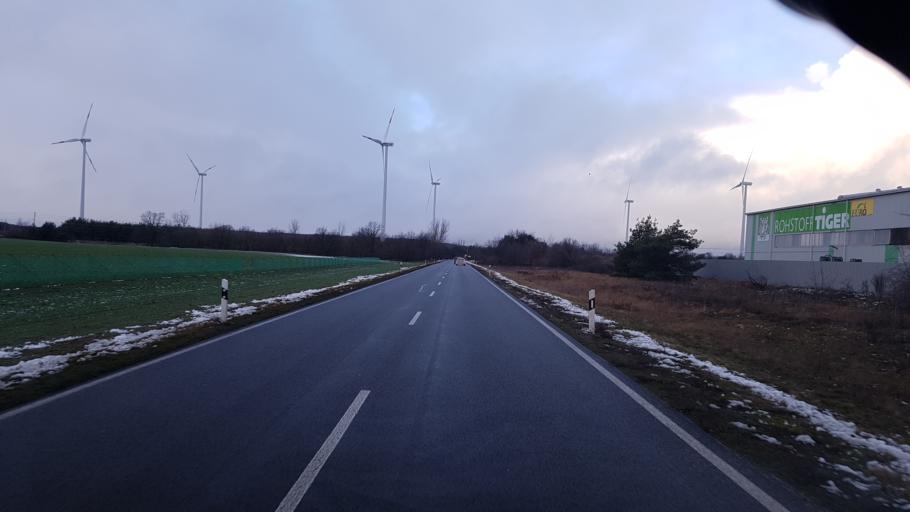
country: DE
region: Brandenburg
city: Heinersbruck
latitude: 51.7815
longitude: 14.4735
